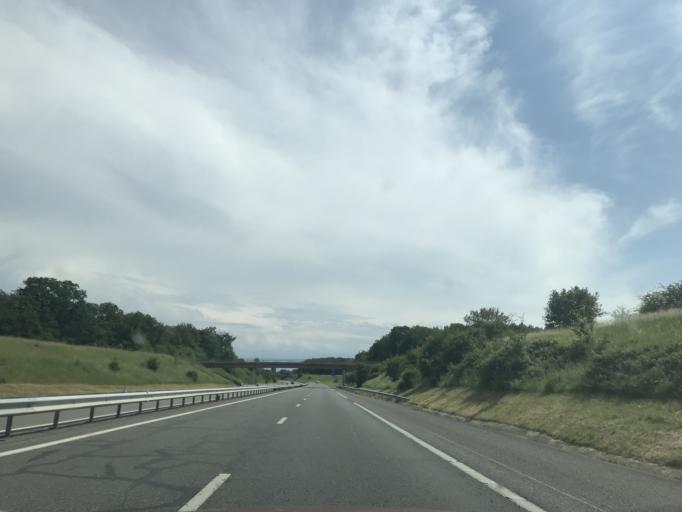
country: FR
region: Centre
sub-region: Departement du Cher
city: Orval
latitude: 46.7631
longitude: 2.4076
